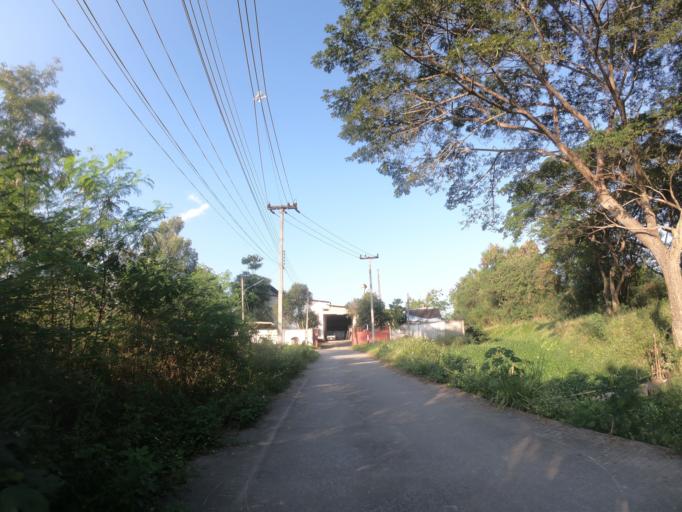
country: TH
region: Chiang Mai
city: Chiang Mai
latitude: 18.7405
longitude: 98.9780
